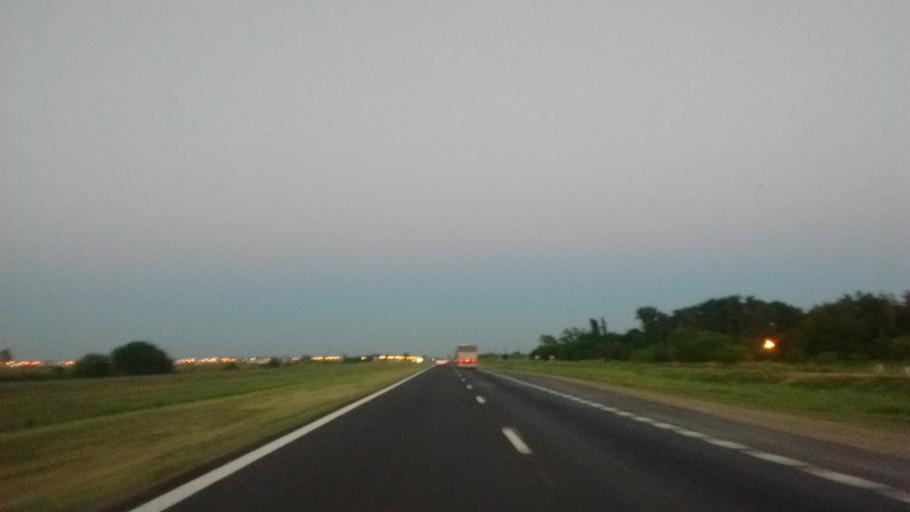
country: AR
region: Santa Fe
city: Roldan
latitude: -32.9320
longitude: -60.8633
